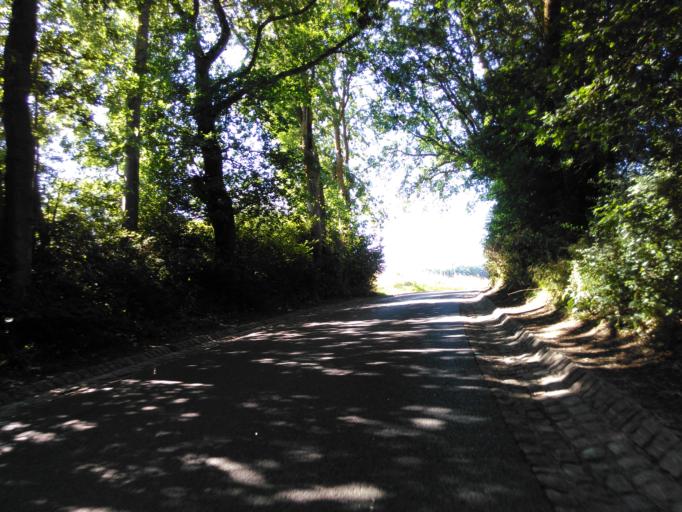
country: LU
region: Luxembourg
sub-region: Canton de Capellen
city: Dippach
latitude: 49.5605
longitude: 5.9773
